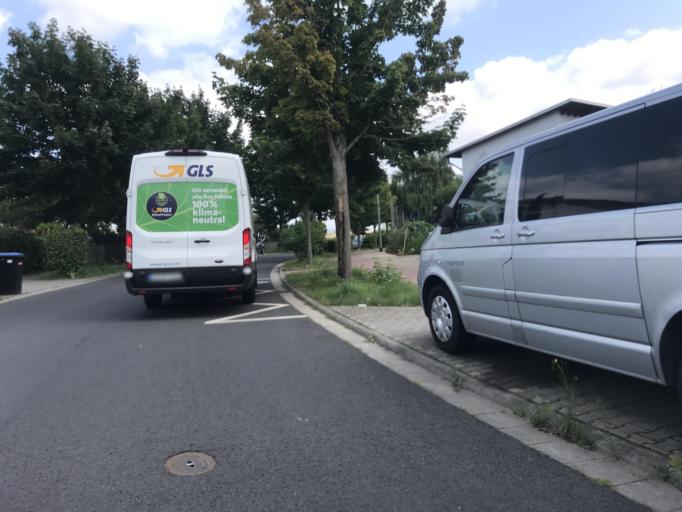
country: DE
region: Hesse
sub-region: Regierungsbezirk Darmstadt
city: Hochheim am Main
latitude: 50.0158
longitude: 8.3728
